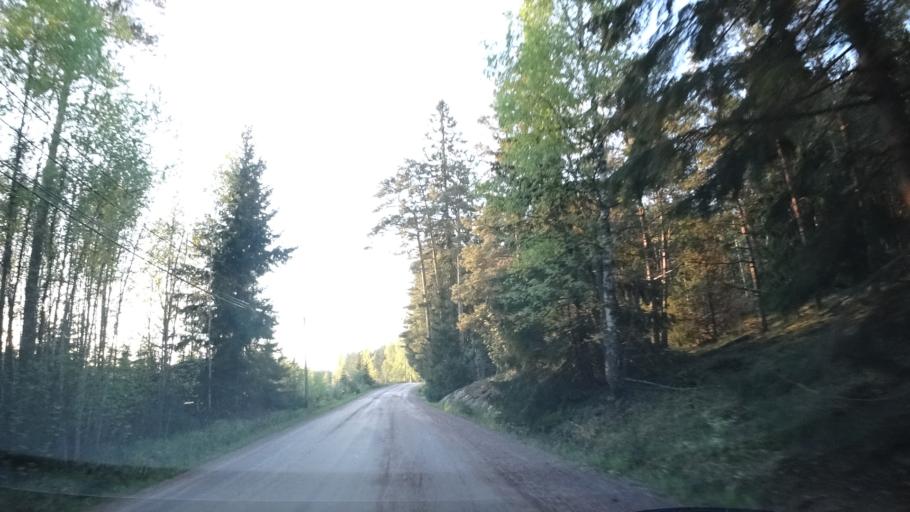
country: FI
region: Uusimaa
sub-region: Helsinki
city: Siuntio
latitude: 60.0695
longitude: 24.2059
